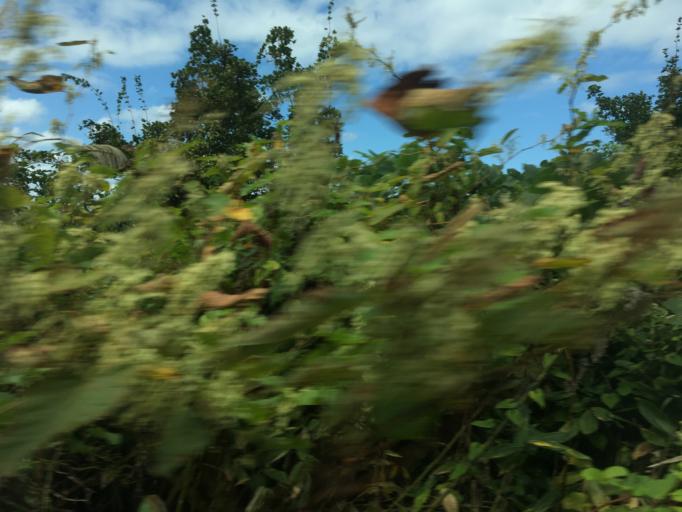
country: JP
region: Aomori
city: Shimokizukuri
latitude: 40.7737
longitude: 140.1857
